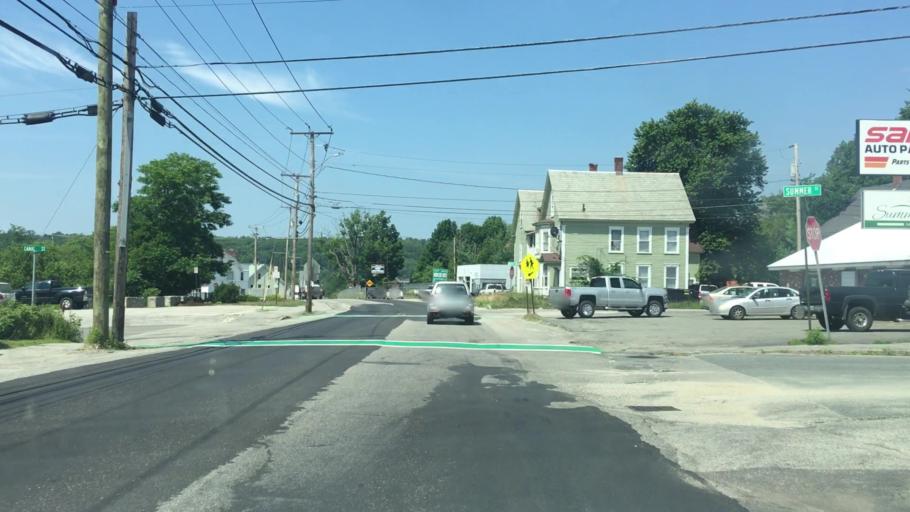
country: US
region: New Hampshire
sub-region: Sullivan County
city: Newport
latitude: 43.3656
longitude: -72.1691
